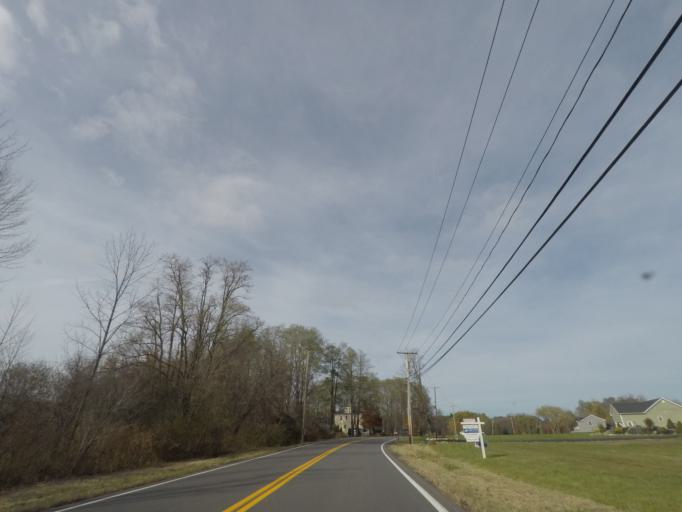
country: US
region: New York
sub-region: Schenectady County
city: Rotterdam
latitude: 42.7560
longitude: -73.9865
